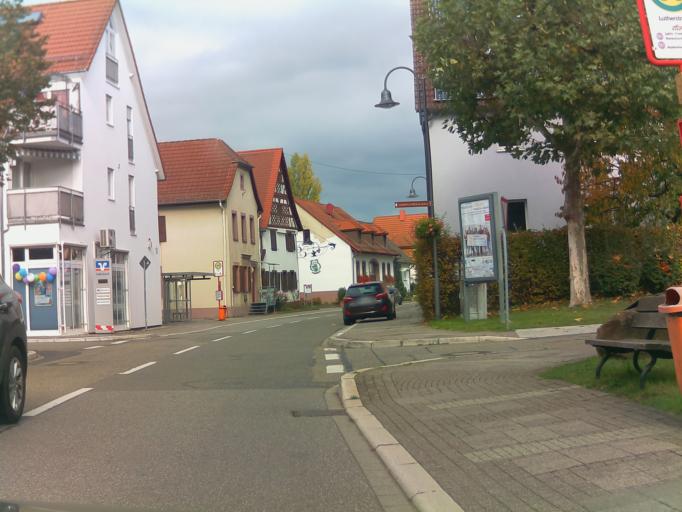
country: DE
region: Baden-Wuerttemberg
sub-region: Karlsruhe Region
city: Weingarten
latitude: 49.0920
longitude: 8.5099
